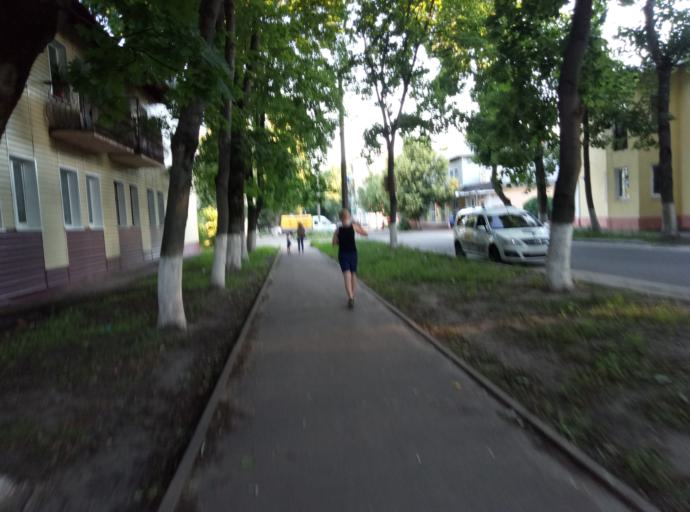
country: RU
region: Kursk
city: Kursk
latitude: 51.6727
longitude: 36.1522
